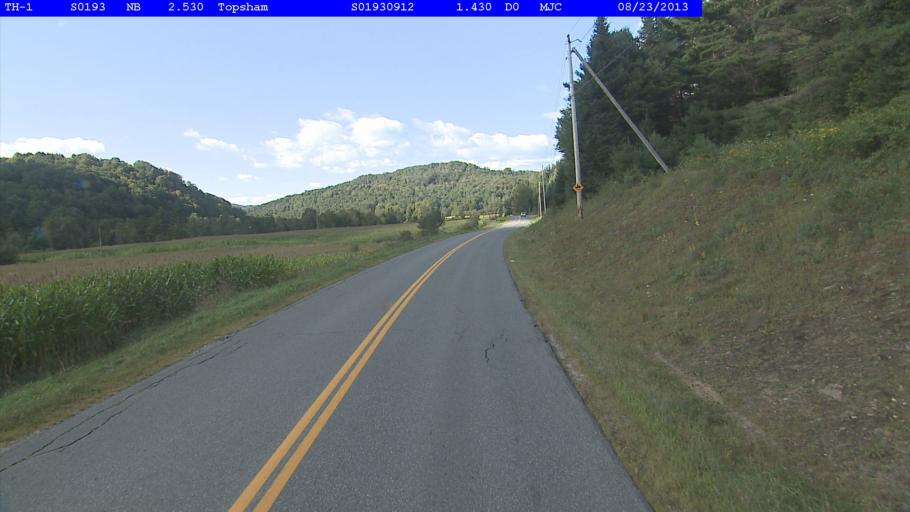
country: US
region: New Hampshire
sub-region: Grafton County
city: Haverhill
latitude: 44.0906
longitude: -72.2226
